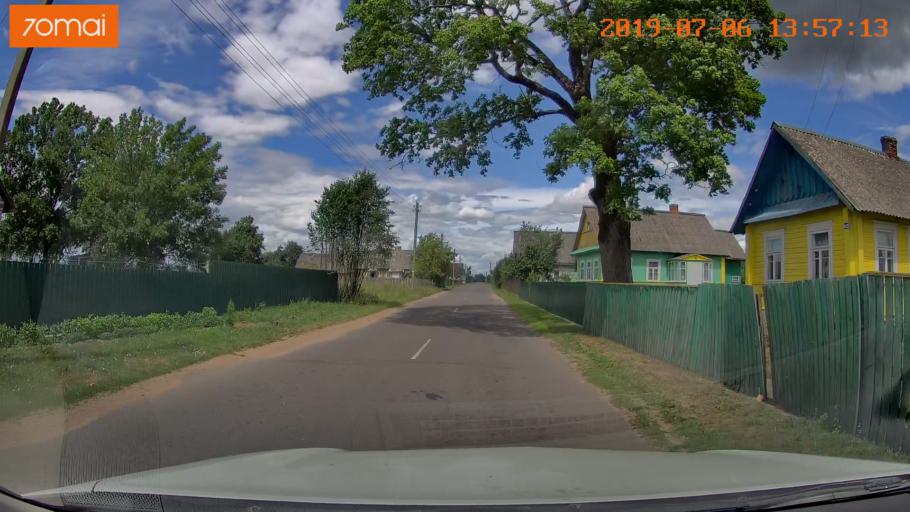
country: BY
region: Minsk
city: Ivyanyets
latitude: 53.7722
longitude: 26.8058
